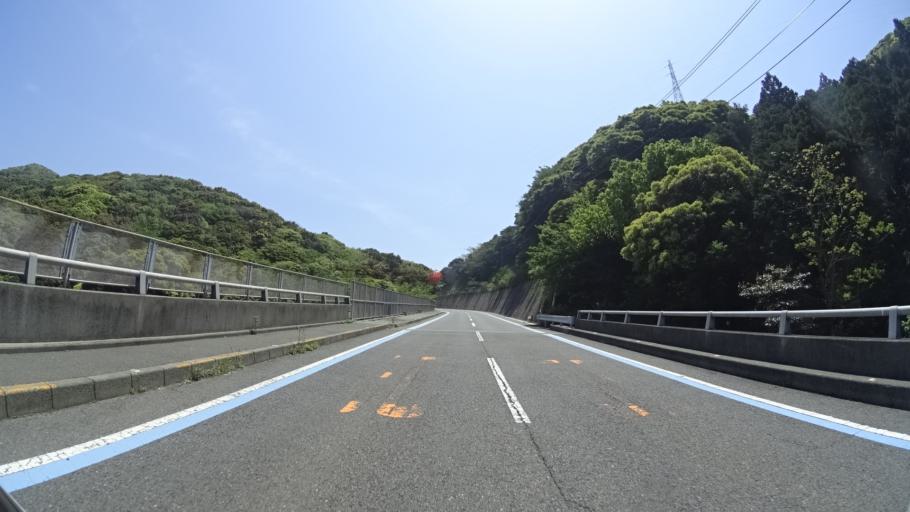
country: JP
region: Ehime
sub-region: Nishiuwa-gun
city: Ikata-cho
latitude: 33.4156
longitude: 132.1763
